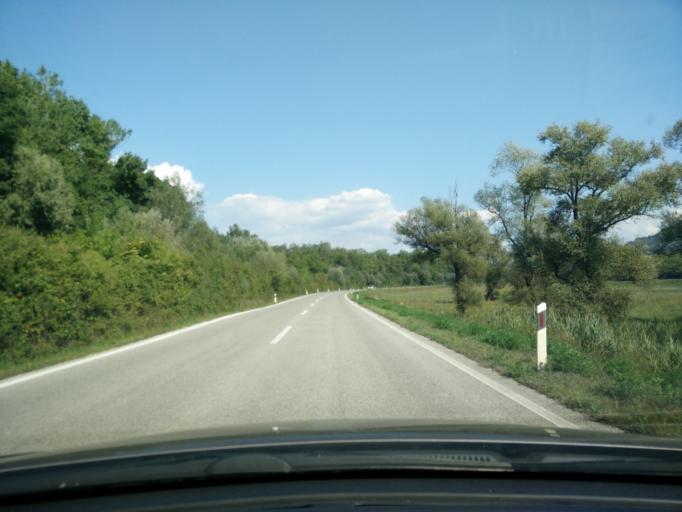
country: HR
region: Istarska
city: Karojba
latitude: 45.3457
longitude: 13.7972
